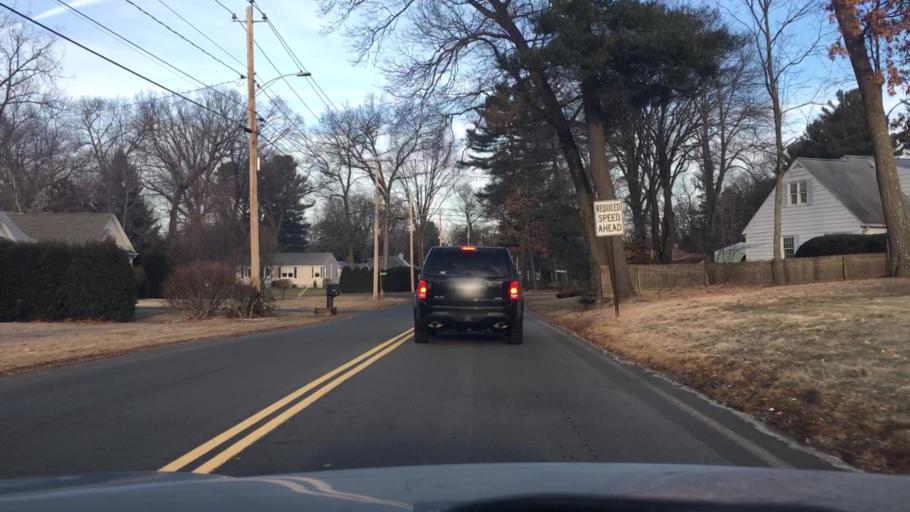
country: US
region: Massachusetts
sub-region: Hampden County
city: Westfield
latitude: 42.1343
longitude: -72.7245
